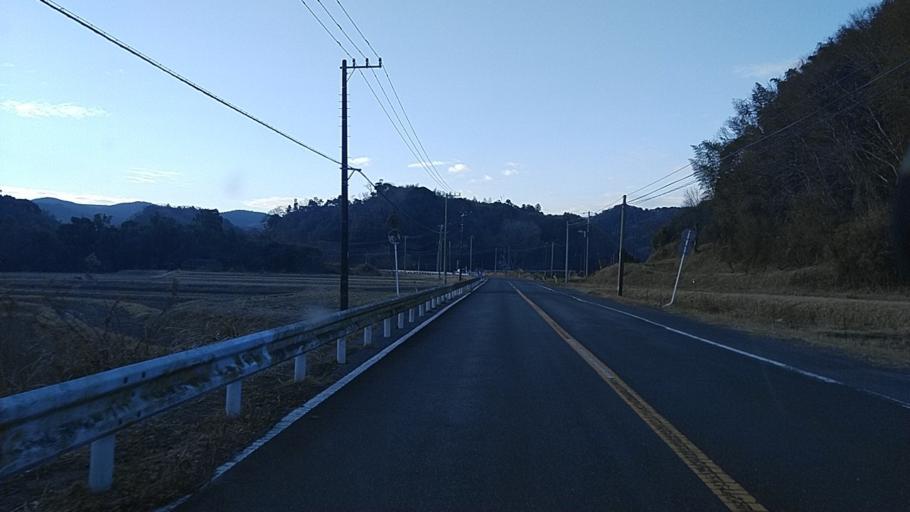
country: JP
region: Chiba
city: Kimitsu
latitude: 35.2831
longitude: 139.9238
